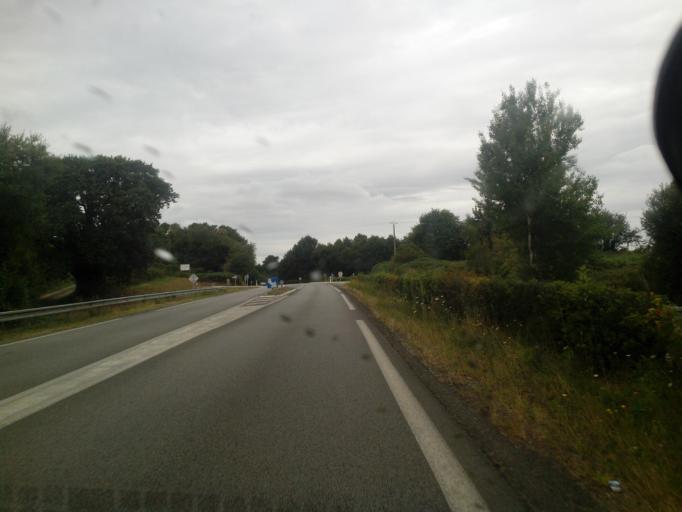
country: FR
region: Brittany
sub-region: Departement du Morbihan
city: Kervignac
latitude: 47.7584
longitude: -3.2471
